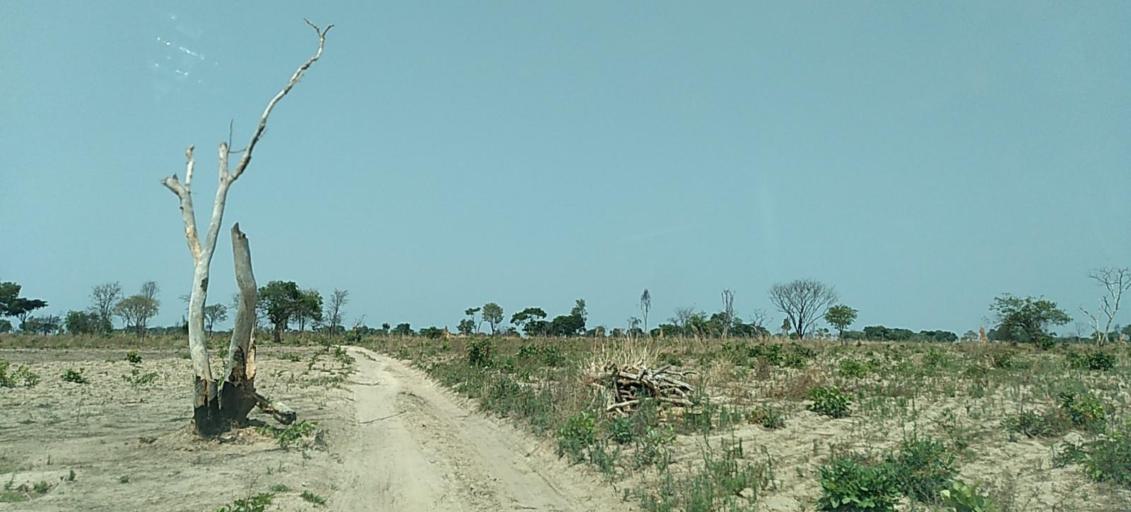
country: ZM
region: Copperbelt
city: Mpongwe
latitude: -13.8631
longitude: 28.0547
